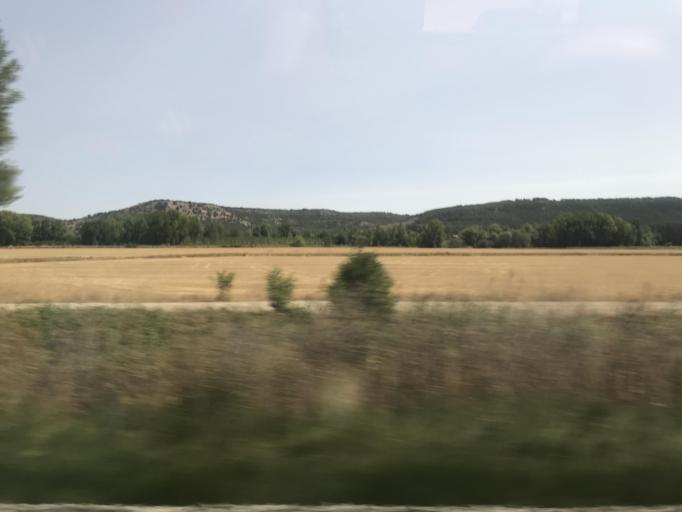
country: ES
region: Castille and Leon
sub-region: Provincia de Burgos
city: Villaldemiro
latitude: 42.2376
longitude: -3.9755
